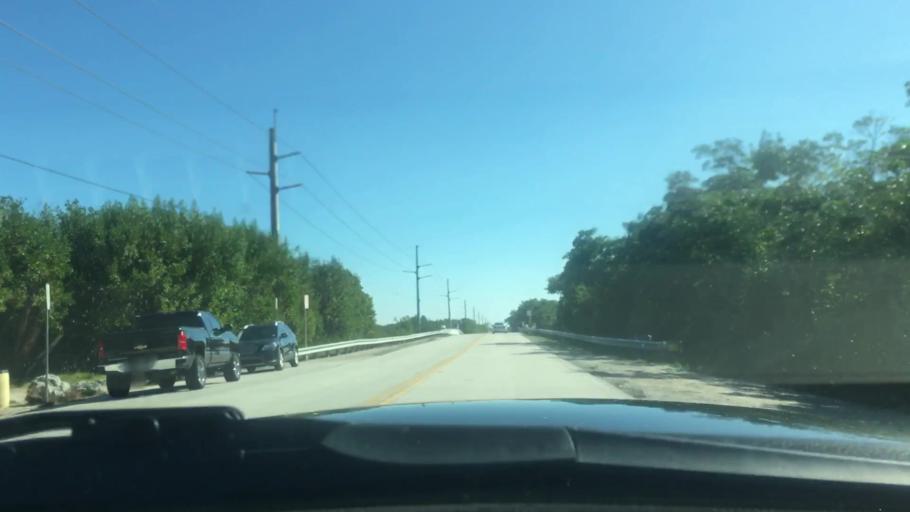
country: US
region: Florida
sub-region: Monroe County
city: North Key Largo
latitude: 25.2841
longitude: -80.3594
